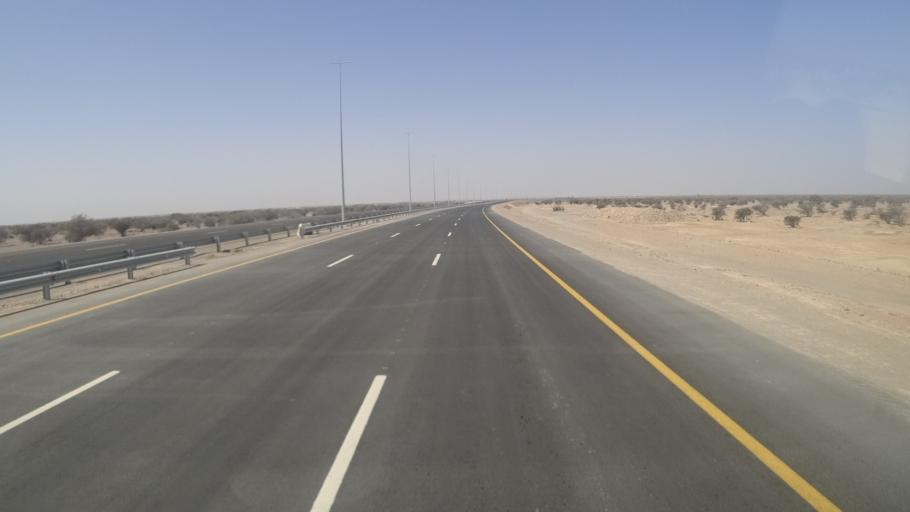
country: OM
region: Ash Sharqiyah
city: Sur
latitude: 22.2733
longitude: 59.2536
